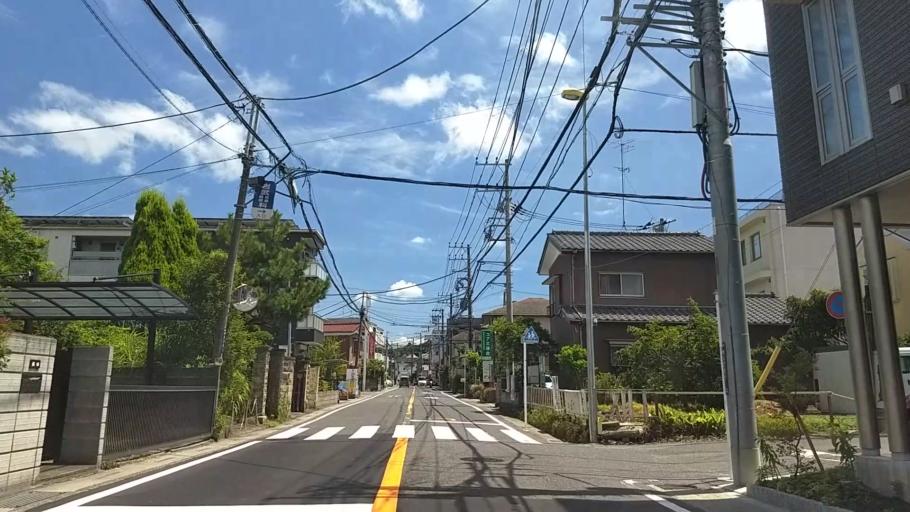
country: JP
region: Kanagawa
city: Kamakura
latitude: 35.3444
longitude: 139.5336
